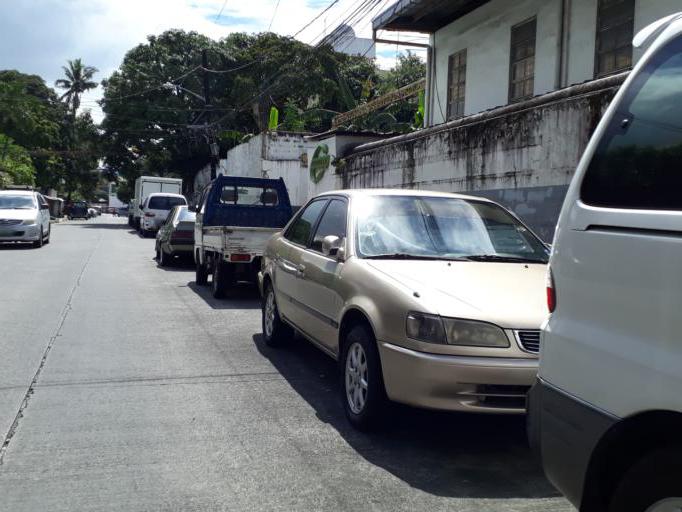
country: PH
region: Calabarzon
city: Del Monte
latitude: 14.6320
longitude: 121.0016
